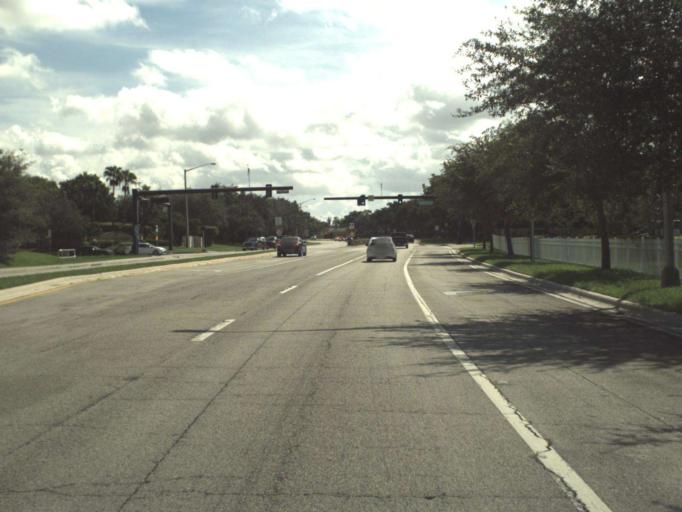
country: US
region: Florida
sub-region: Broward County
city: Coral Springs
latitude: 26.2332
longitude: -80.2940
